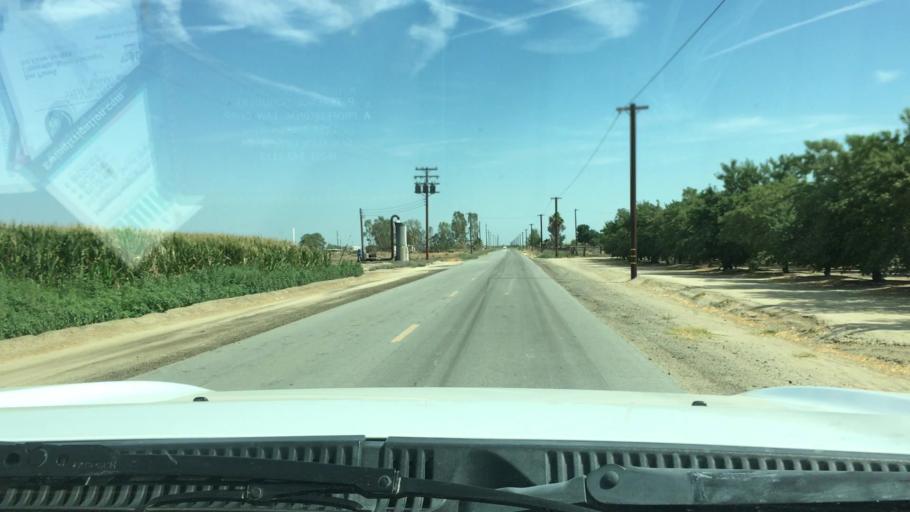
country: US
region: California
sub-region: Kern County
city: Buttonwillow
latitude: 35.4266
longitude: -119.3762
